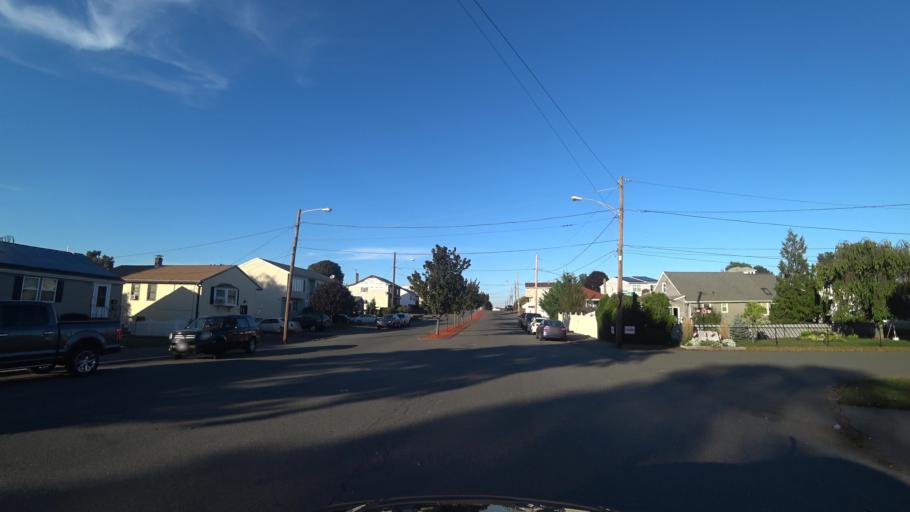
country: US
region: Massachusetts
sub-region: Suffolk County
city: Revere
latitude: 42.4192
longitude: -71.0116
